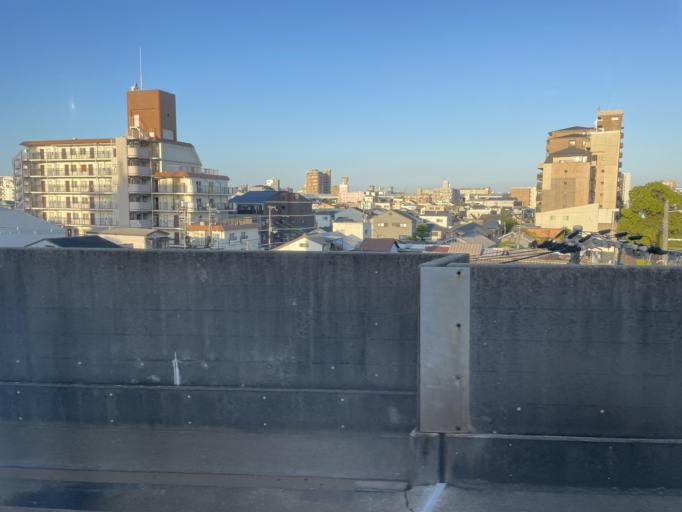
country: JP
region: Osaka
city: Matsubara
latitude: 34.6309
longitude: 135.5297
